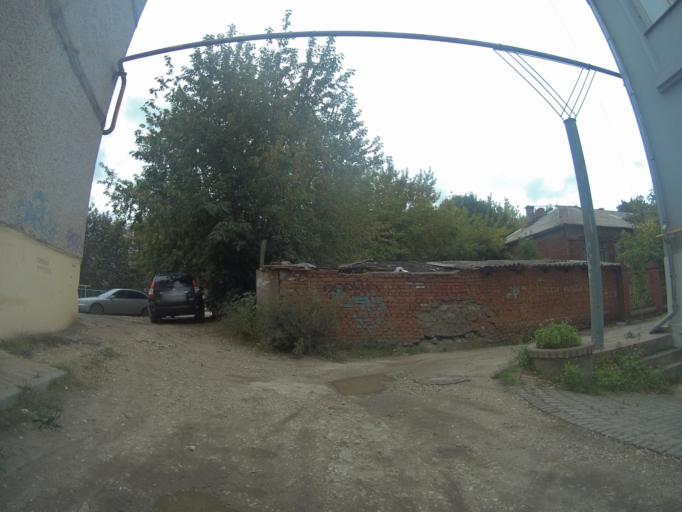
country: RU
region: Vladimir
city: Vladimir
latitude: 56.1150
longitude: 40.3544
